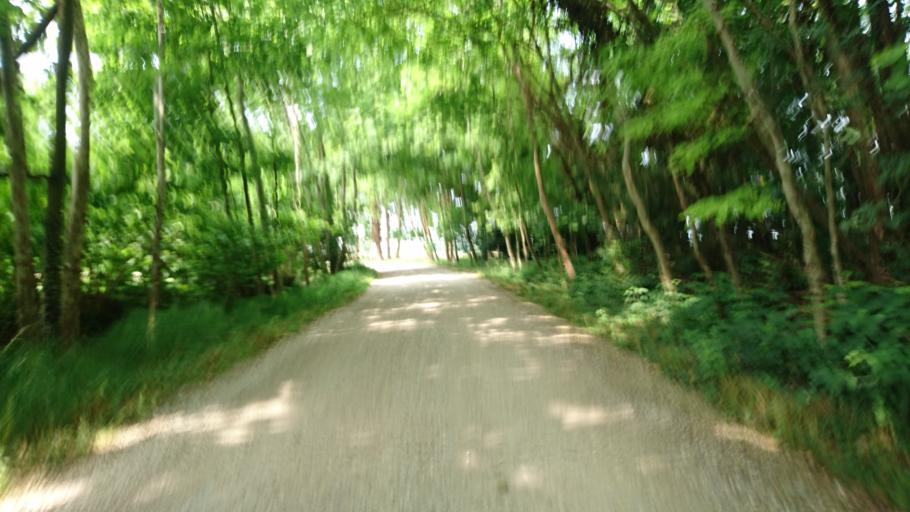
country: IT
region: Veneto
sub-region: Provincia di Padova
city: Legnaro
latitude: 45.3271
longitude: 11.9562
